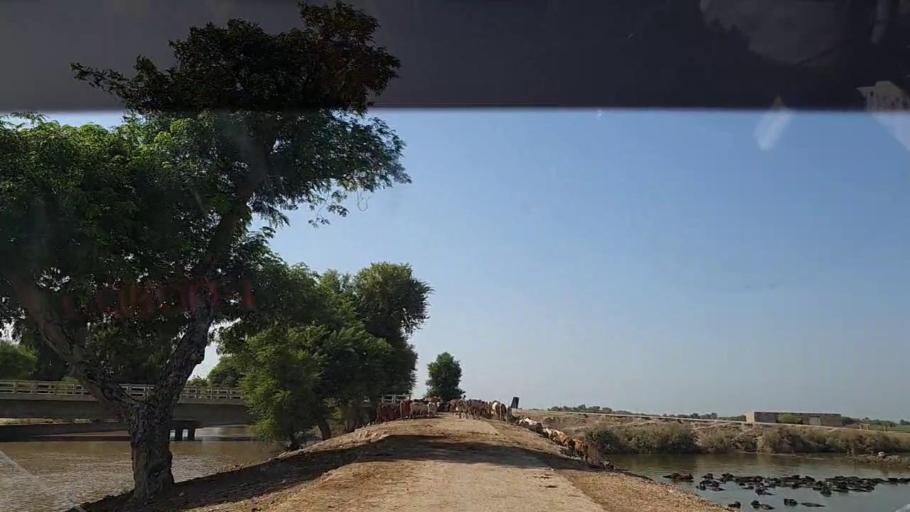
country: PK
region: Sindh
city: Ghauspur
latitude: 28.2007
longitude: 69.0416
